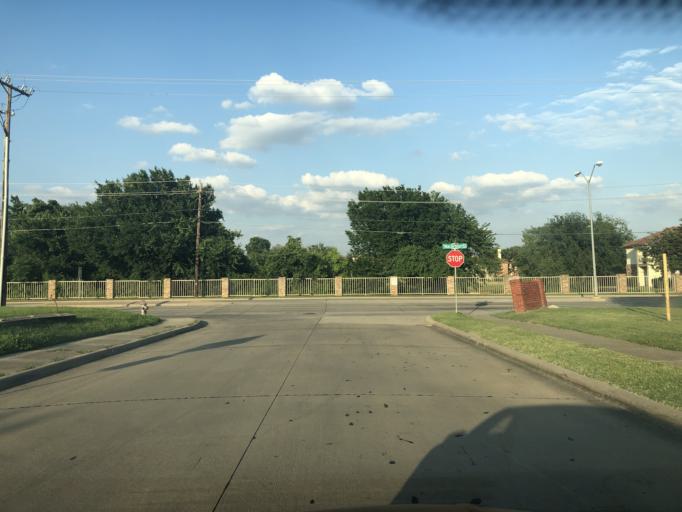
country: US
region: Texas
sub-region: Dallas County
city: Irving
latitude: 32.7917
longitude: -96.9602
